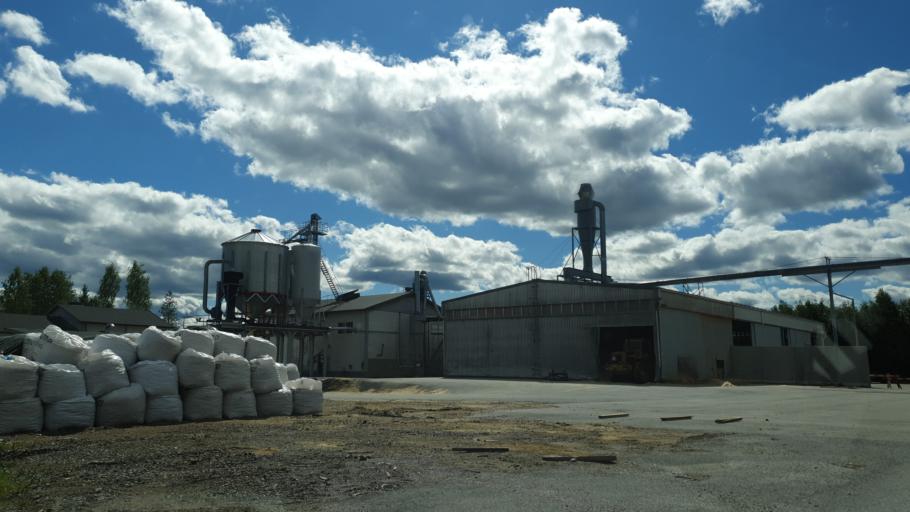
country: FI
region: Kainuu
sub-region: Kehys-Kainuu
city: Kuhmo
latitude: 64.1345
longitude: 29.4688
